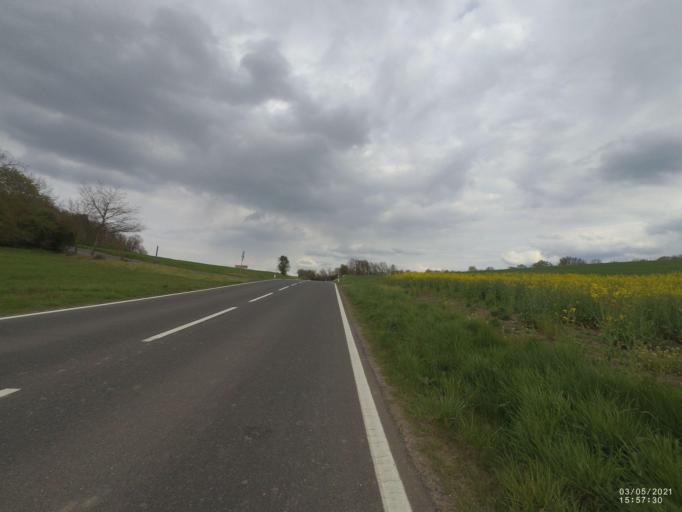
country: DE
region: Rheinland-Pfalz
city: Lonnig
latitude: 50.3421
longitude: 7.4193
